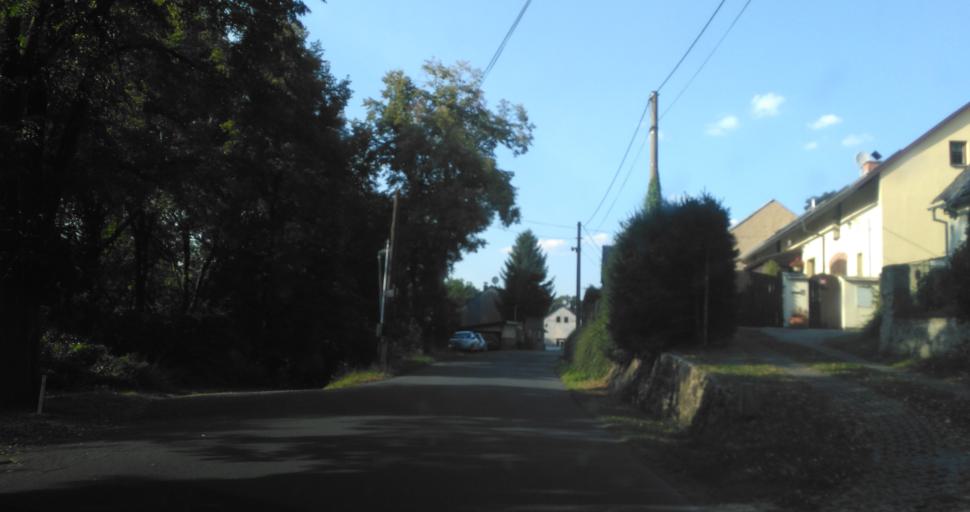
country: CZ
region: Central Bohemia
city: Zebrak
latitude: 49.8893
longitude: 13.8832
